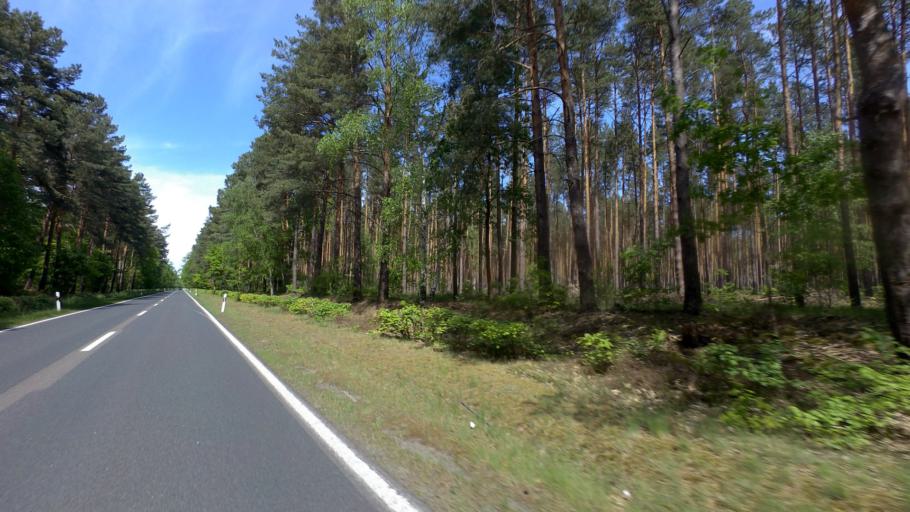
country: DE
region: Brandenburg
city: Sperenberg
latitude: 52.1172
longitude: 13.3696
